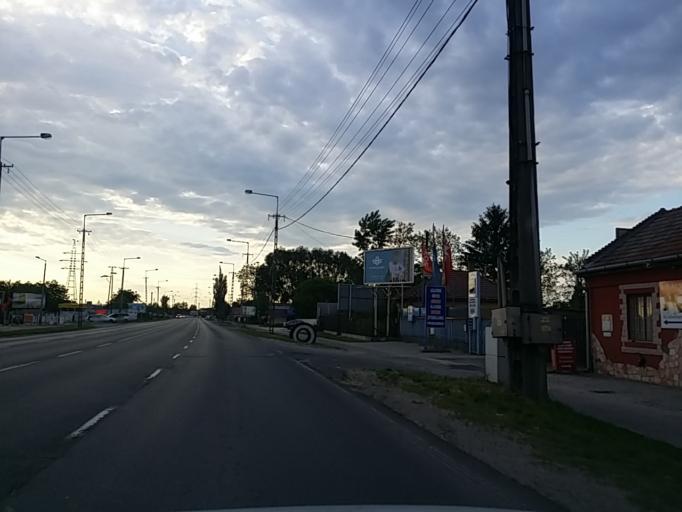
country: HU
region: Bacs-Kiskun
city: Kecskemet
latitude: 46.9266
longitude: 19.6674
